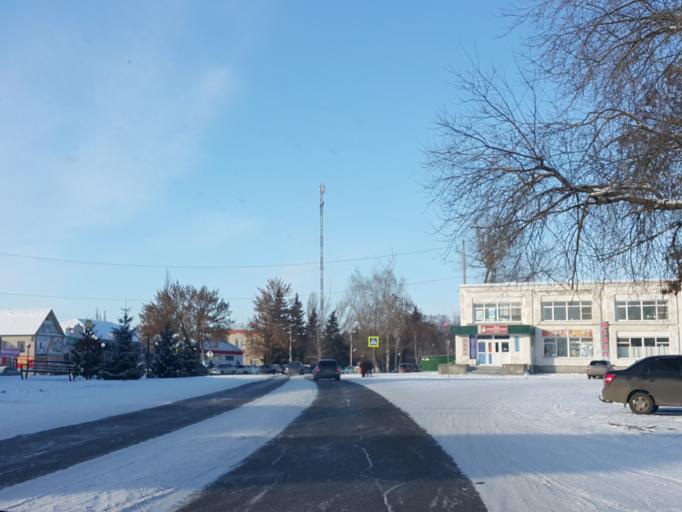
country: RU
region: Tambov
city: Znamenka
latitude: 52.4149
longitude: 41.4433
